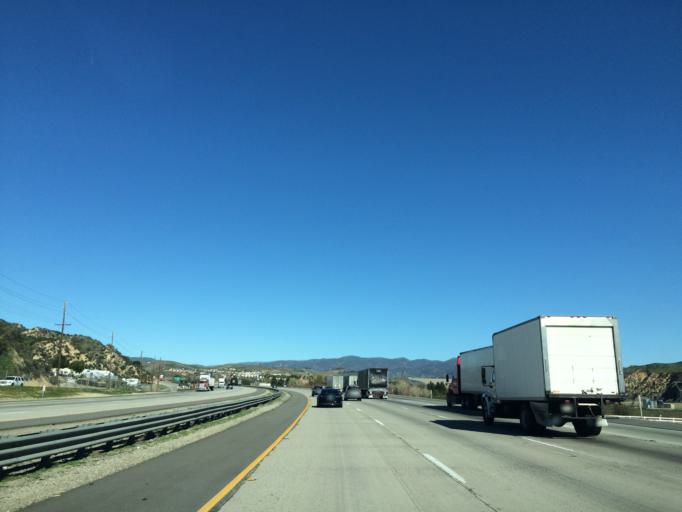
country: US
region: California
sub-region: Los Angeles County
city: Castaic
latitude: 34.4804
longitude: -118.6144
